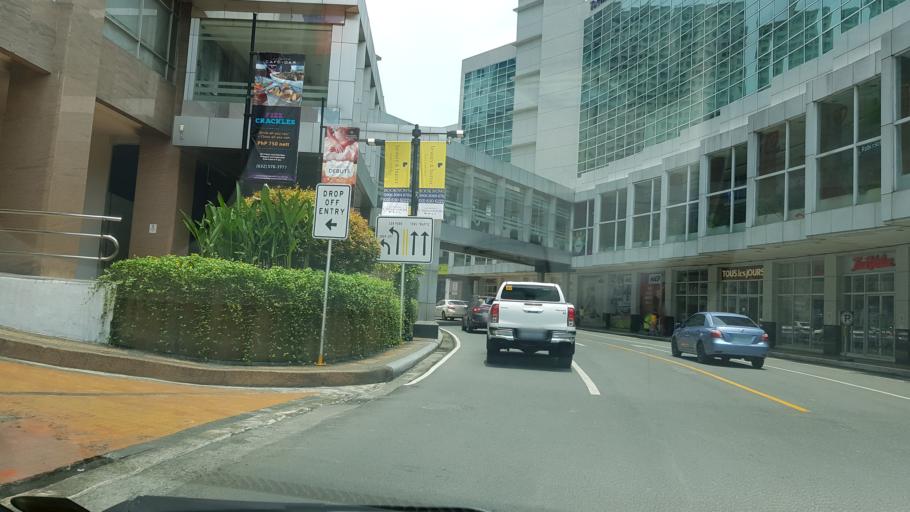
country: PH
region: Metro Manila
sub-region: Marikina
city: Calumpang
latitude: 14.6101
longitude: 121.0806
